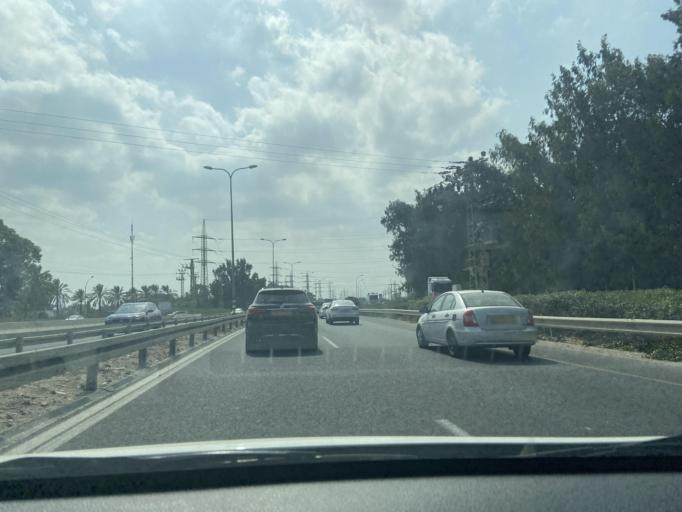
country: IL
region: Northern District
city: `Akko
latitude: 32.8978
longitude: 35.0930
